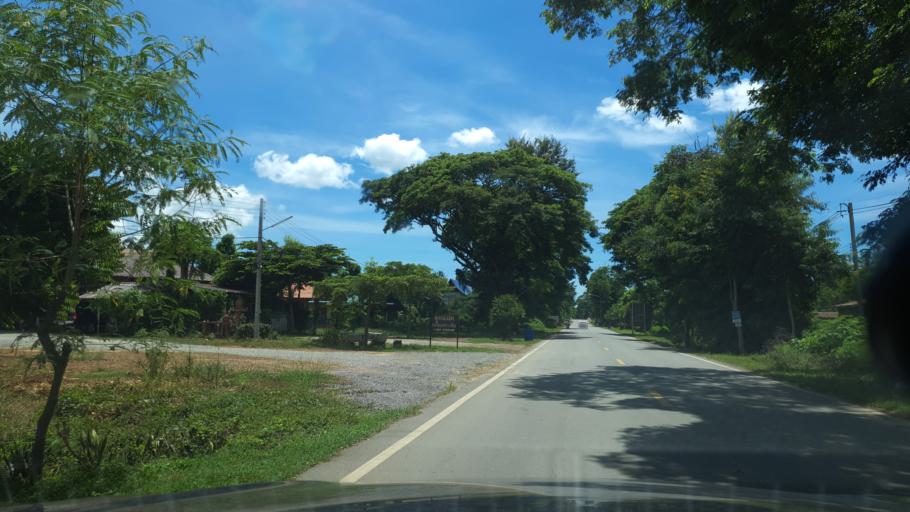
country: TH
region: Sukhothai
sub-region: Amphoe Si Satchanalai
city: Si Satchanalai
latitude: 17.4346
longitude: 99.8017
